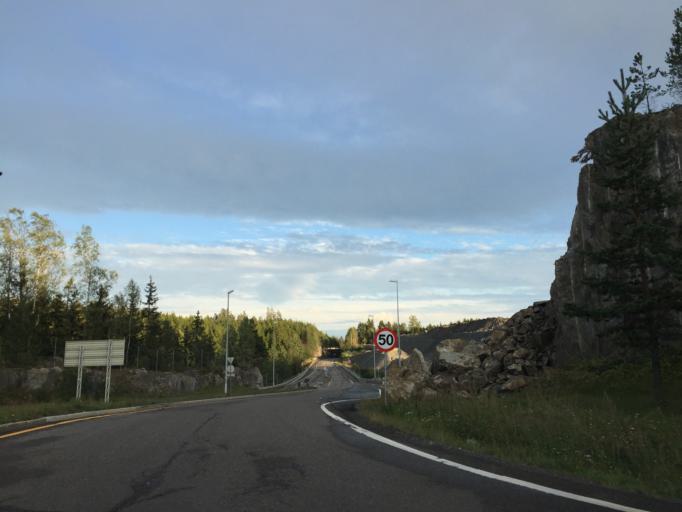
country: NO
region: Akershus
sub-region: Oppegard
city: Kolbotn
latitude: 59.7835
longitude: 10.8403
